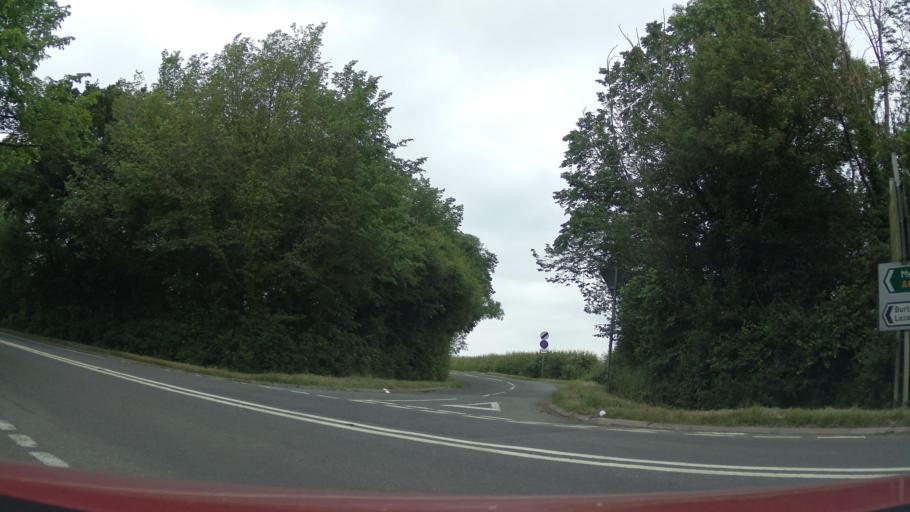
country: GB
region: England
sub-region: Leicestershire
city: Melton Mowbray
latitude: 52.7176
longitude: -0.8294
